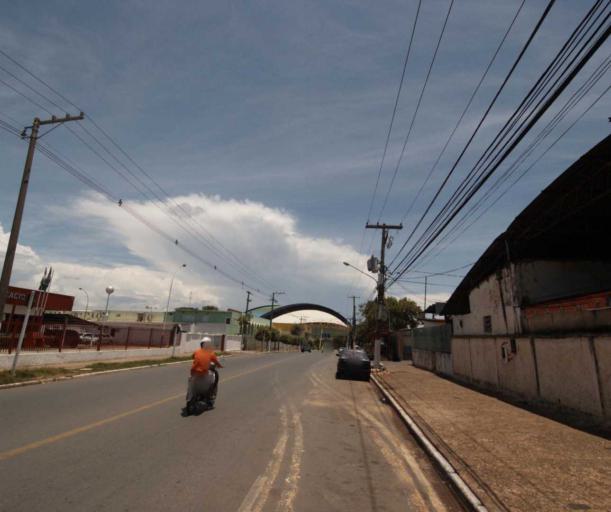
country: BR
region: Mato Grosso
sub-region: Cuiaba
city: Cuiaba
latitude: -15.6045
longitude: -56.1269
